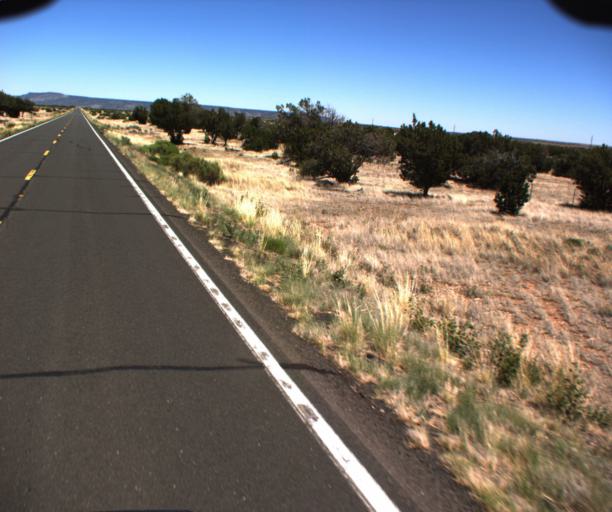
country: US
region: Arizona
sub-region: Coconino County
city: LeChee
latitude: 34.7507
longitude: -111.0385
